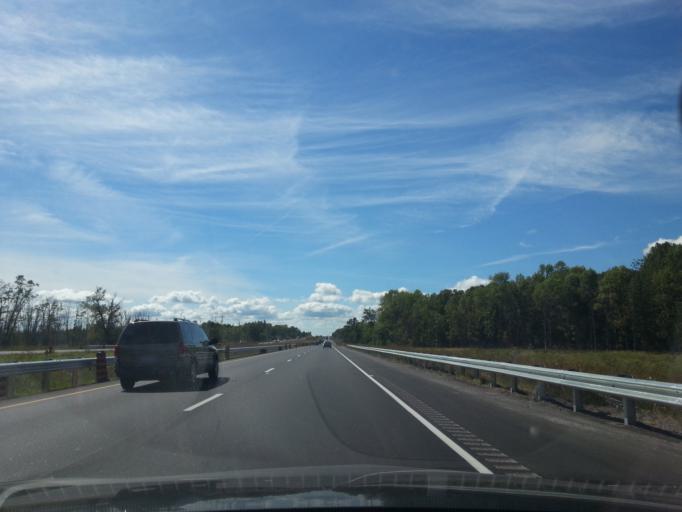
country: CA
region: Ontario
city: Skatepark
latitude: 44.2777
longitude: -76.8293
